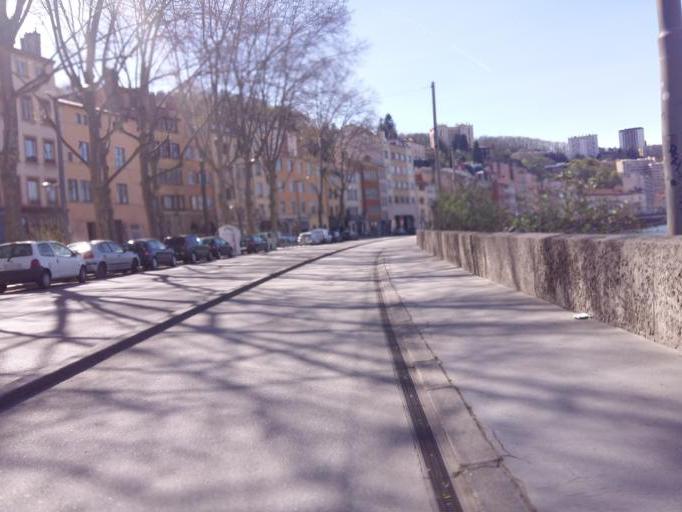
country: FR
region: Rhone-Alpes
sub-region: Departement du Rhone
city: Caluire-et-Cuire
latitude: 45.7666
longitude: 4.8198
